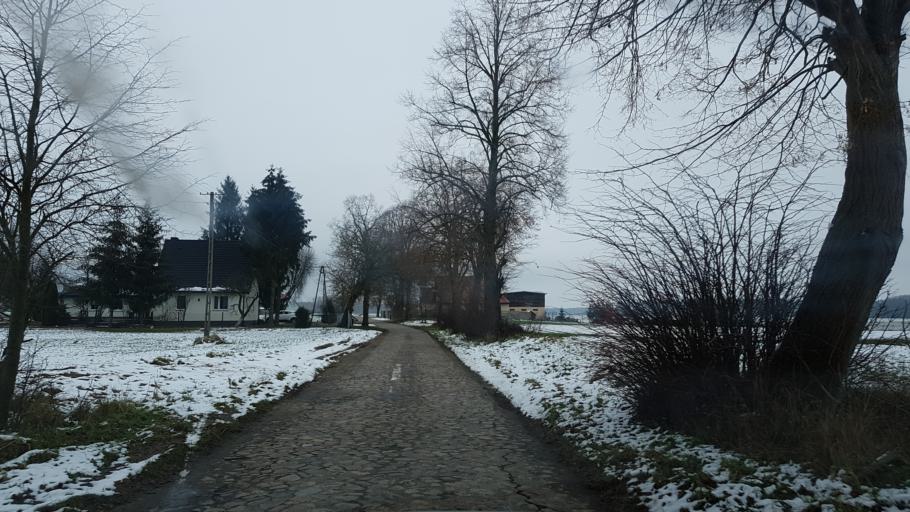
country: PL
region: West Pomeranian Voivodeship
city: Trzcinsko Zdroj
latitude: 52.9695
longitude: 14.7178
